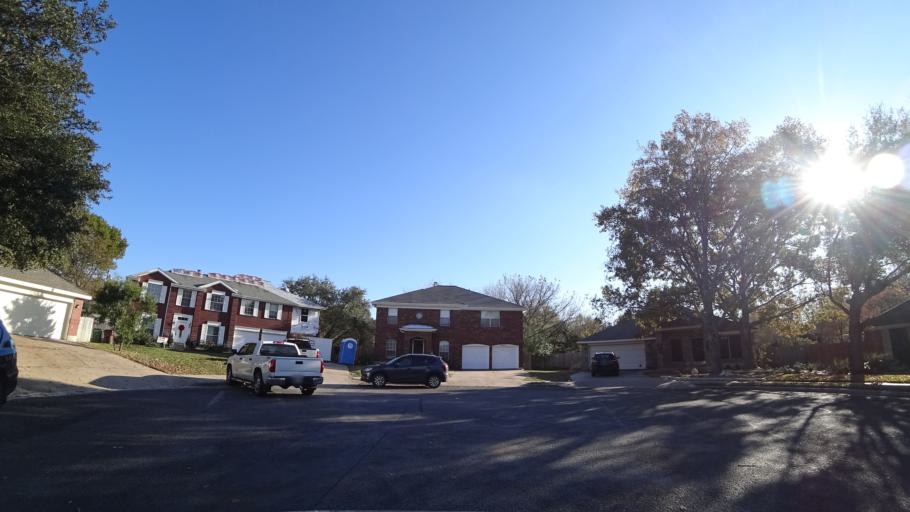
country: US
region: Texas
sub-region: Williamson County
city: Brushy Creek
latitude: 30.5027
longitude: -97.7421
